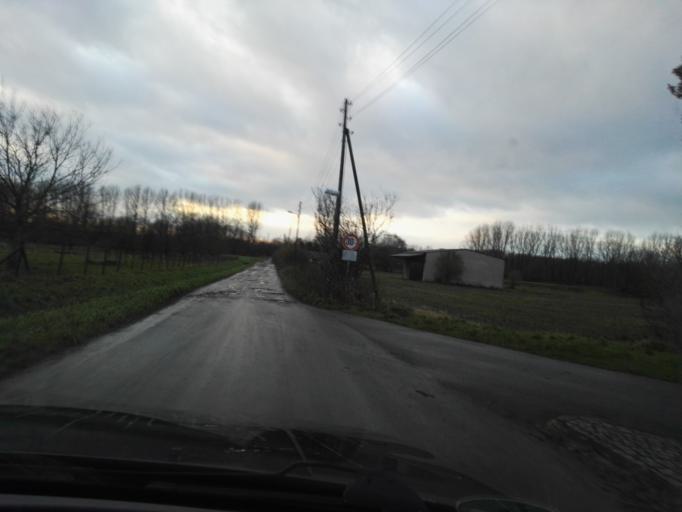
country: DE
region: Lower Saxony
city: Leiferde
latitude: 52.2249
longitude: 10.4553
